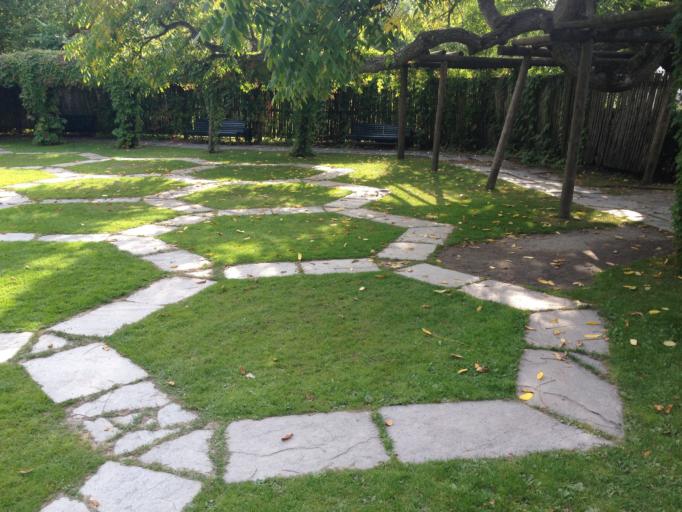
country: SE
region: OErebro
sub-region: Orebro Kommun
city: Orebro
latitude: 59.2709
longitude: 15.2287
